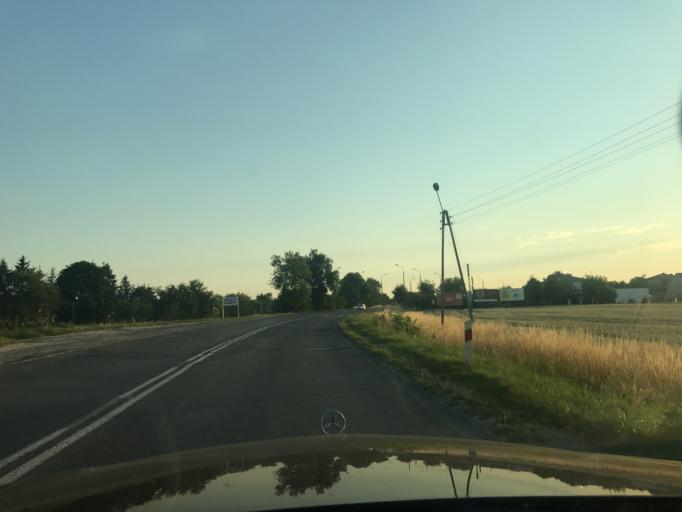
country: PL
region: Lublin Voivodeship
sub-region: Powiat lubartowski
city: Lubartow
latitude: 51.4748
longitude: 22.6100
